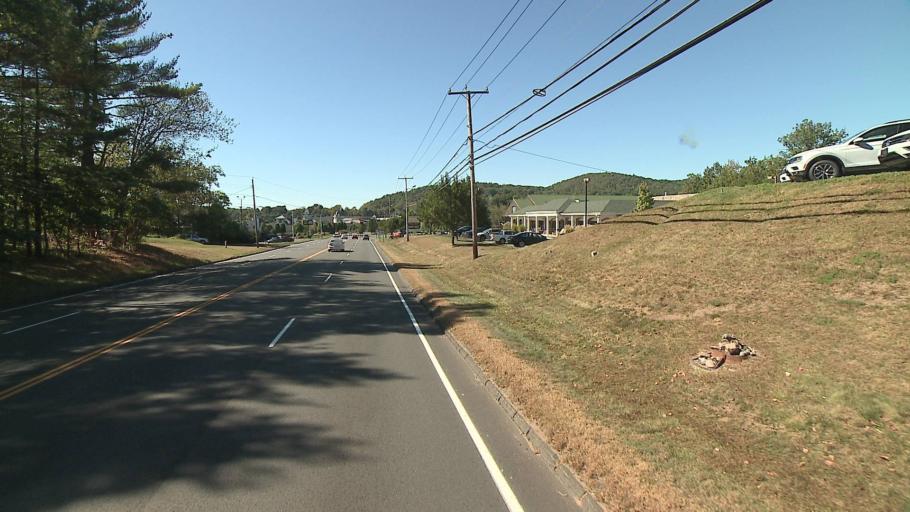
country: US
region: Connecticut
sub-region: Hartford County
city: Canton Valley
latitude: 41.8230
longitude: -72.8777
